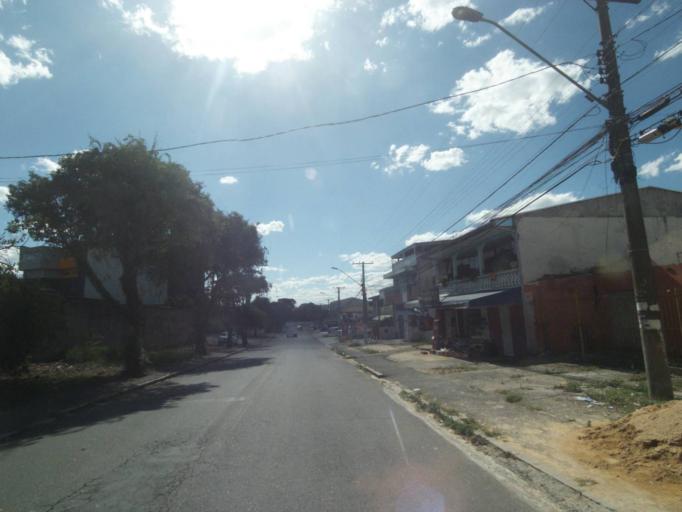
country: BR
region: Parana
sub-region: Curitiba
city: Curitiba
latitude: -25.5109
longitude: -49.3266
